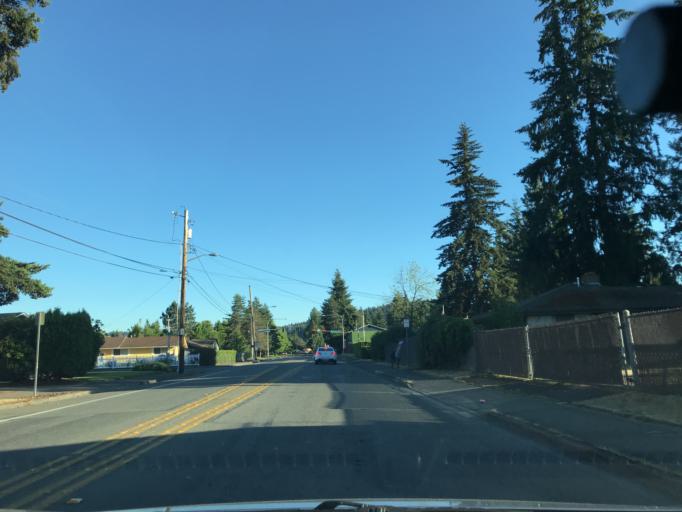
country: US
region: Washington
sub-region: King County
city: Auburn
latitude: 47.2841
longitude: -122.2080
